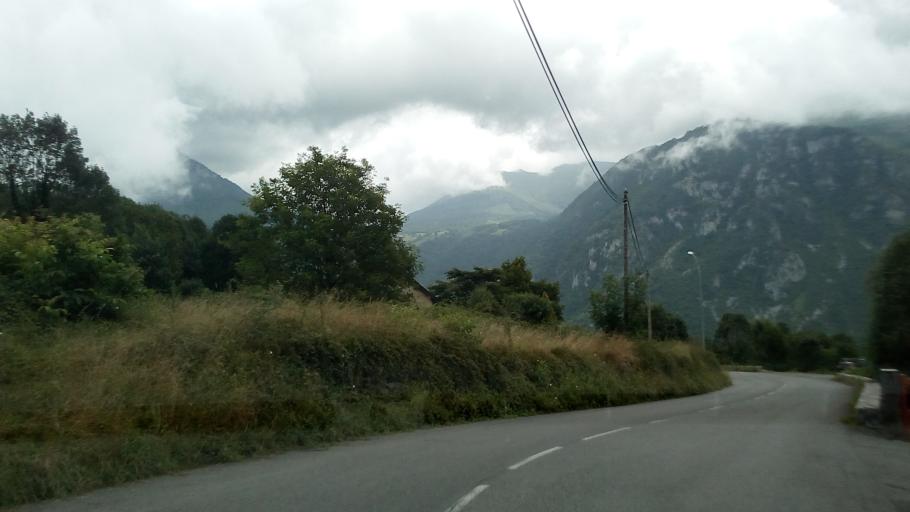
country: FR
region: Aquitaine
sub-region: Departement des Pyrenees-Atlantiques
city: Louvie-Juzon
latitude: 43.0606
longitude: -0.4437
